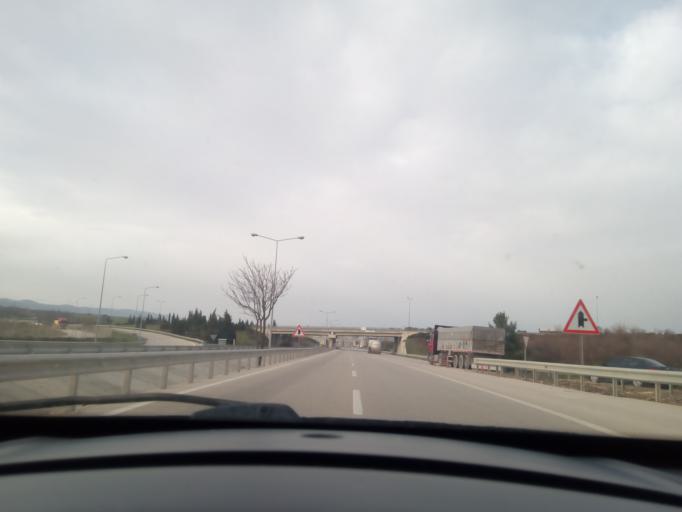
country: TR
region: Bursa
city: Gorukle
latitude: 40.2259
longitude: 28.7859
